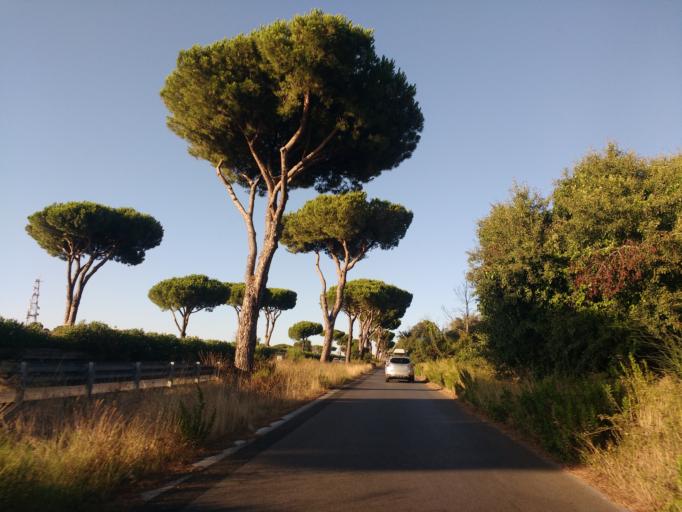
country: IT
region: Latium
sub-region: Citta metropolitana di Roma Capitale
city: Vitinia
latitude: 41.7620
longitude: 12.3793
